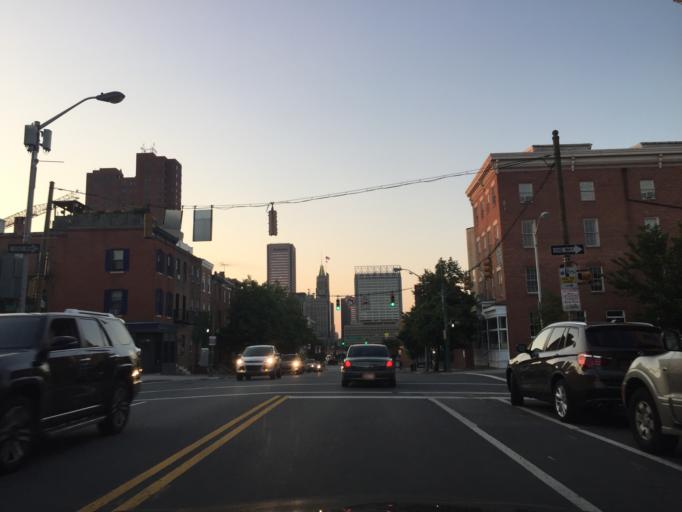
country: US
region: Maryland
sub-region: City of Baltimore
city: Baltimore
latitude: 39.2797
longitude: -76.6127
